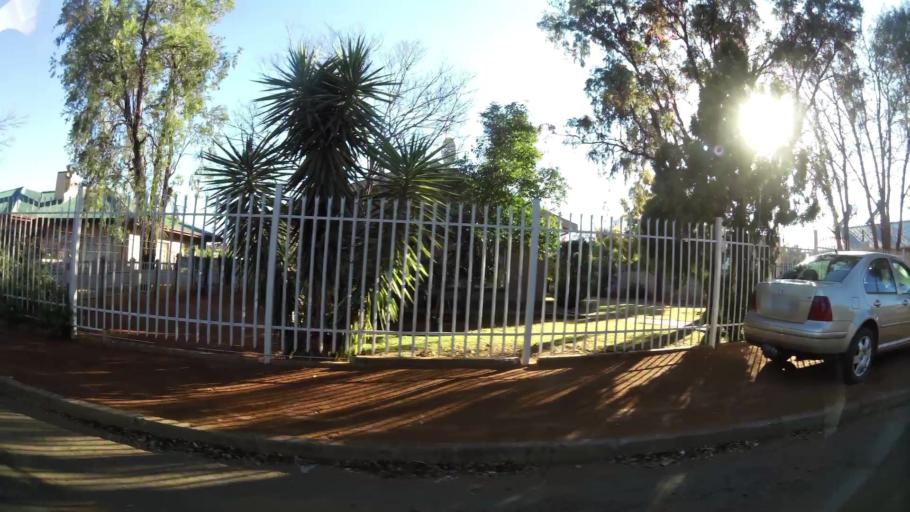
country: ZA
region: Northern Cape
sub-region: Frances Baard District Municipality
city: Kimberley
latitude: -28.7372
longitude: 24.7320
